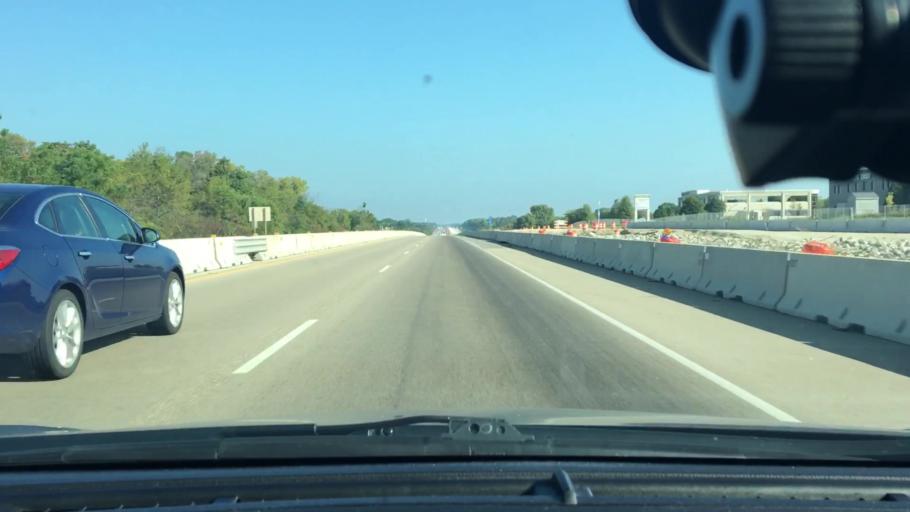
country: US
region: Wisconsin
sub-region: Rock County
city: Janesville
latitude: 42.6735
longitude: -88.9837
